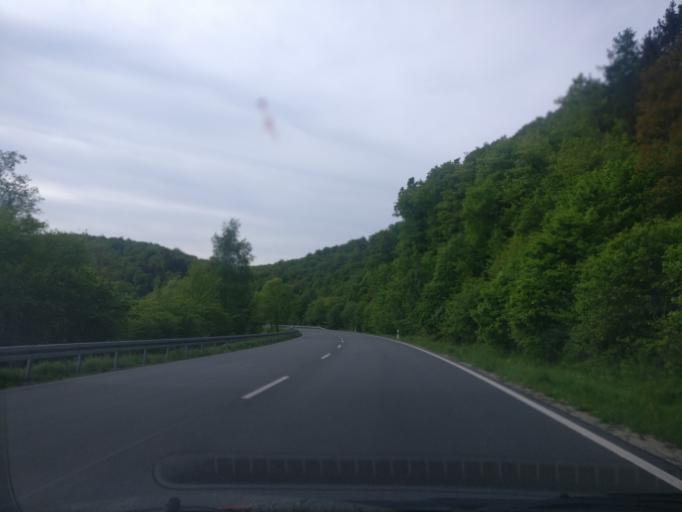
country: DE
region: Hesse
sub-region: Regierungsbezirk Kassel
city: Fuldatal
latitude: 51.3680
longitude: 9.5411
